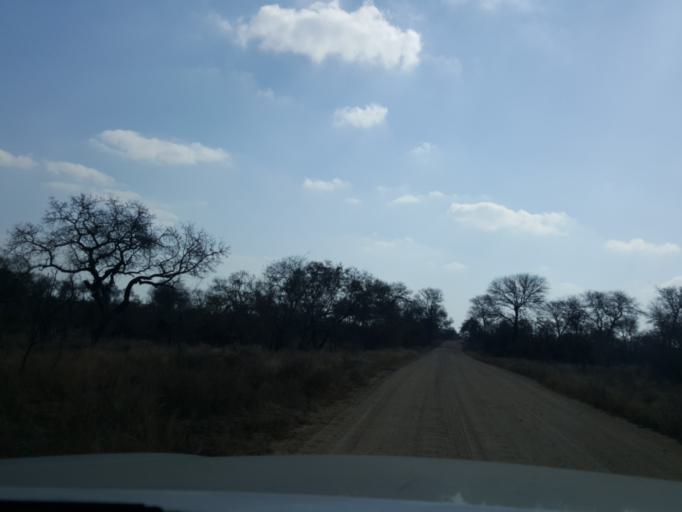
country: ZA
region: Mpumalanga
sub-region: Ehlanzeni District
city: Komatipoort
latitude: -25.2691
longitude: 31.7999
